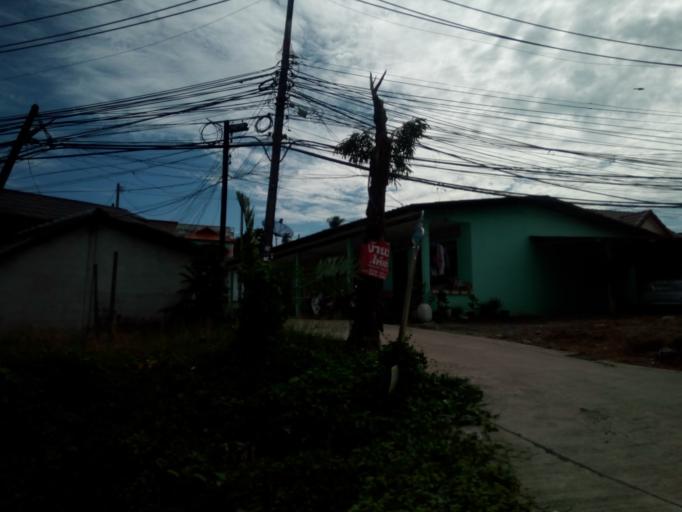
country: TH
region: Phuket
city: Mueang Phuket
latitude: 7.8310
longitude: 98.4003
